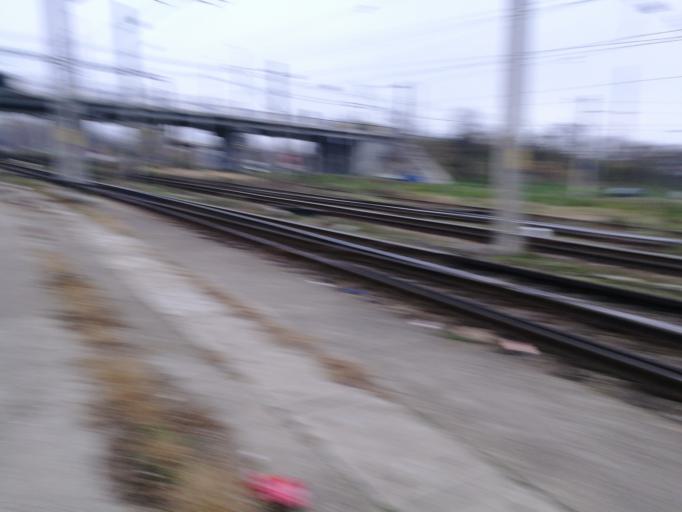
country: RO
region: Suceava
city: Suceava
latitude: 47.6681
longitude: 26.2720
